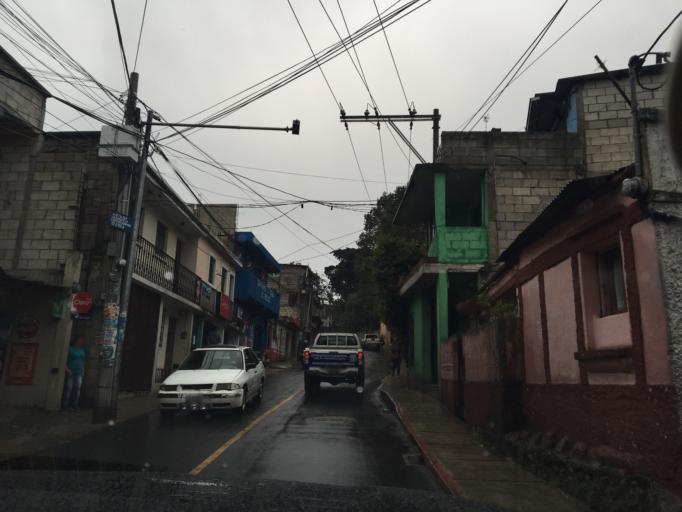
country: GT
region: Guatemala
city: Santa Catarina Pinula
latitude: 14.5647
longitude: -90.4894
